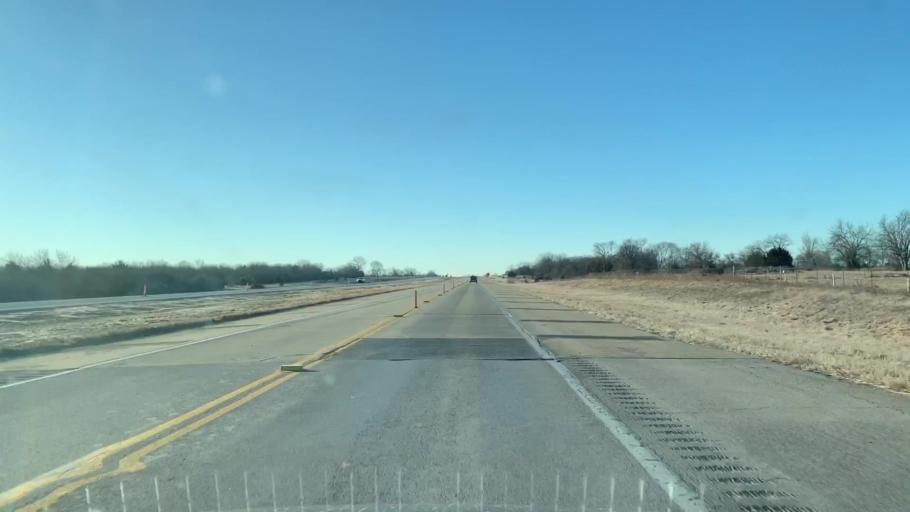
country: US
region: Kansas
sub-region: Bourbon County
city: Fort Scott
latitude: 37.7587
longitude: -94.7050
